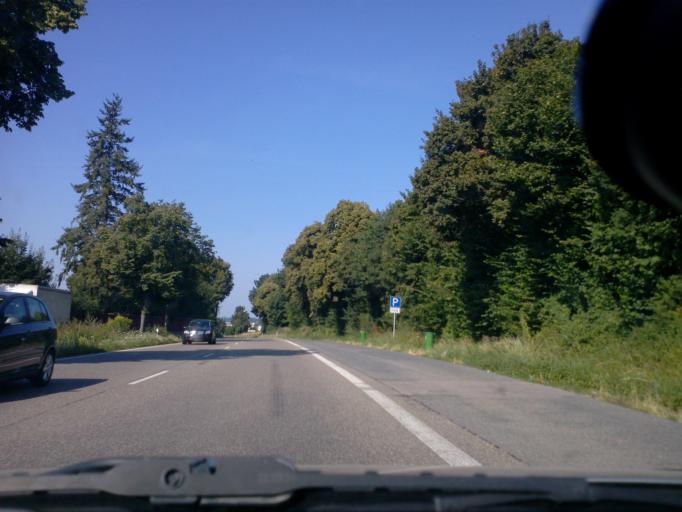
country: DE
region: Baden-Wuerttemberg
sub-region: Karlsruhe Region
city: Bretten
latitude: 49.0430
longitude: 8.7005
